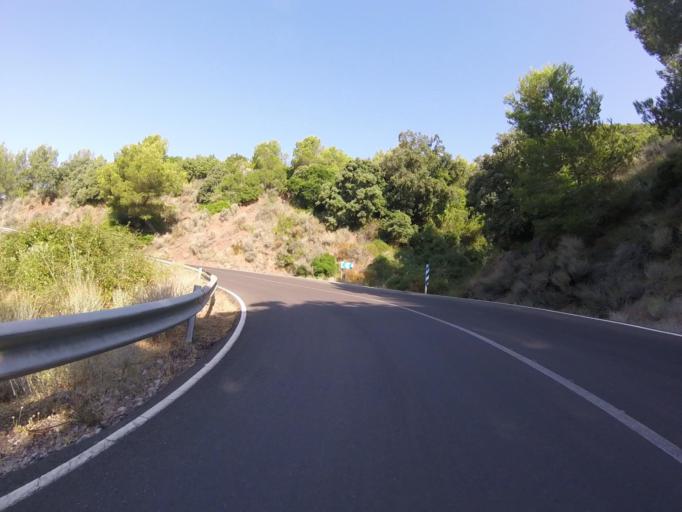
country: ES
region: Valencia
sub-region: Provincia de Castello
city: Benicassim
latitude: 40.0800
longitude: 0.0412
